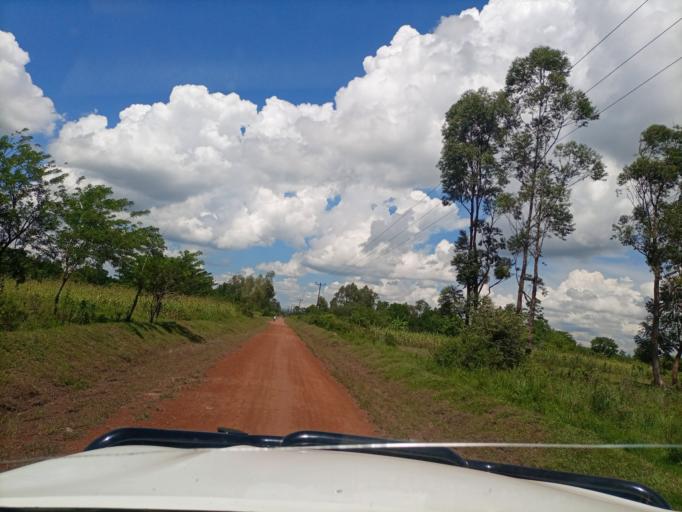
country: UG
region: Eastern Region
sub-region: Tororo District
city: Tororo
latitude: 0.6547
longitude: 33.9987
